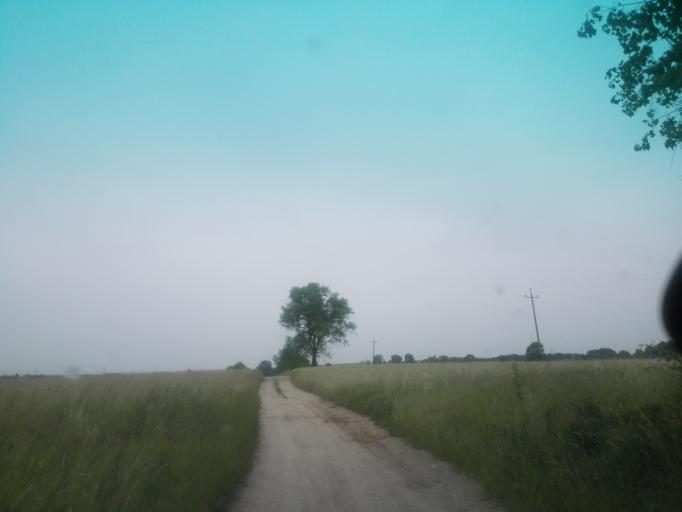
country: PL
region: Silesian Voivodeship
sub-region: Powiat czestochowski
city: Mstow
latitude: 50.7862
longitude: 19.3211
